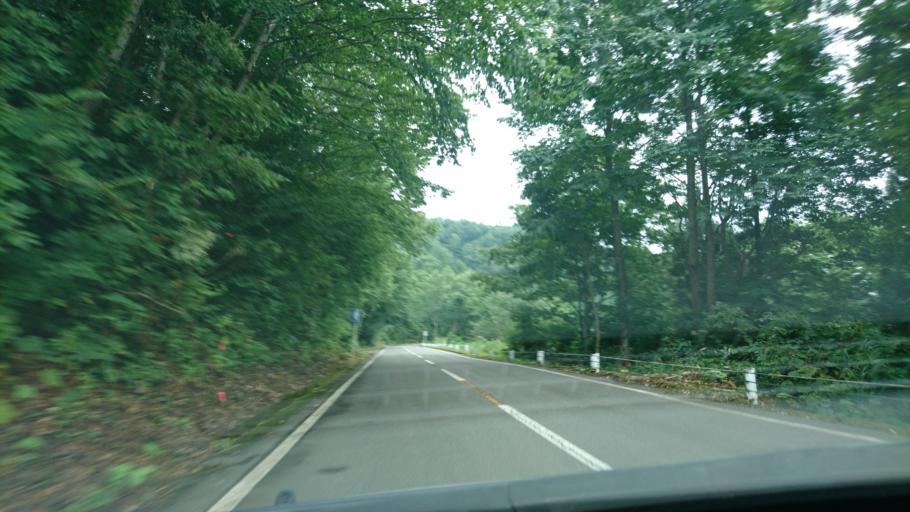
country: JP
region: Akita
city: Yuzawa
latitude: 38.9747
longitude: 140.7223
